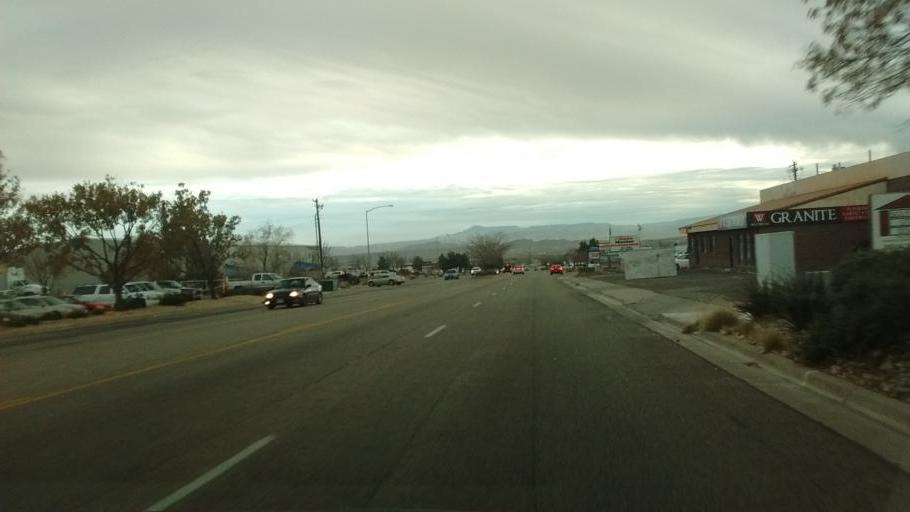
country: US
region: Utah
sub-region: Washington County
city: Washington
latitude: 37.1187
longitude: -113.5208
